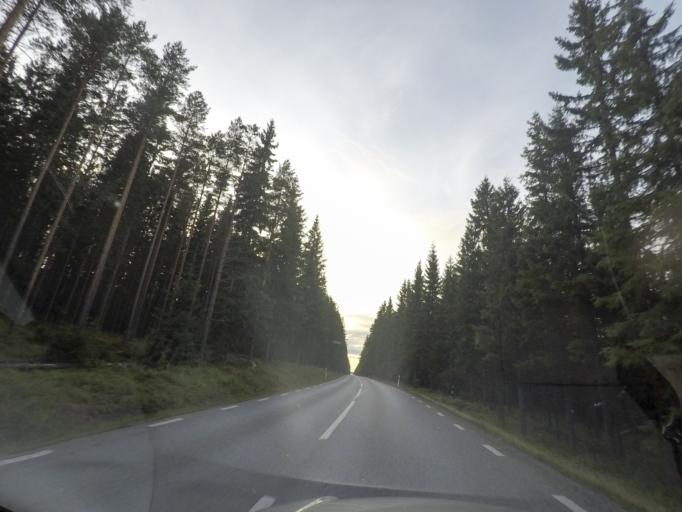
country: SE
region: OErebro
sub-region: Hallefors Kommun
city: Haellefors
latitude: 59.5975
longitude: 14.6718
